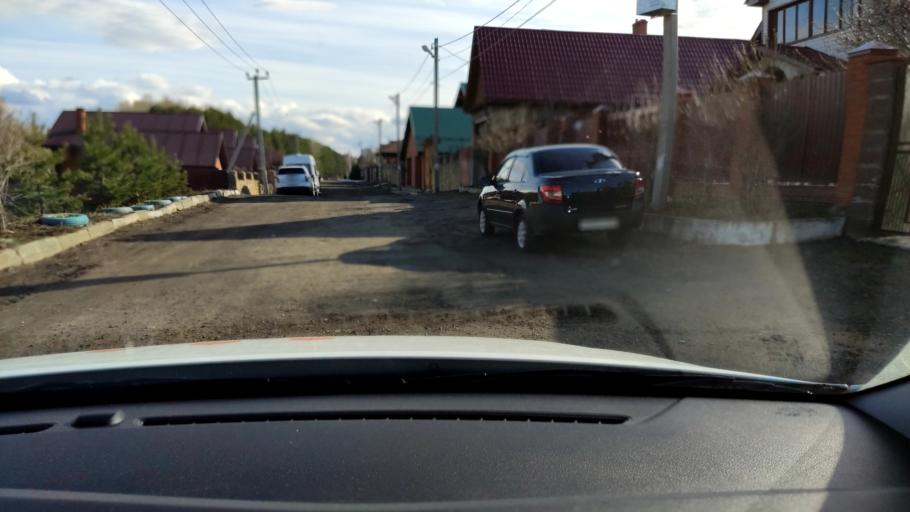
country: RU
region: Tatarstan
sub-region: Gorod Kazan'
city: Kazan
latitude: 55.7816
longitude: 49.2478
